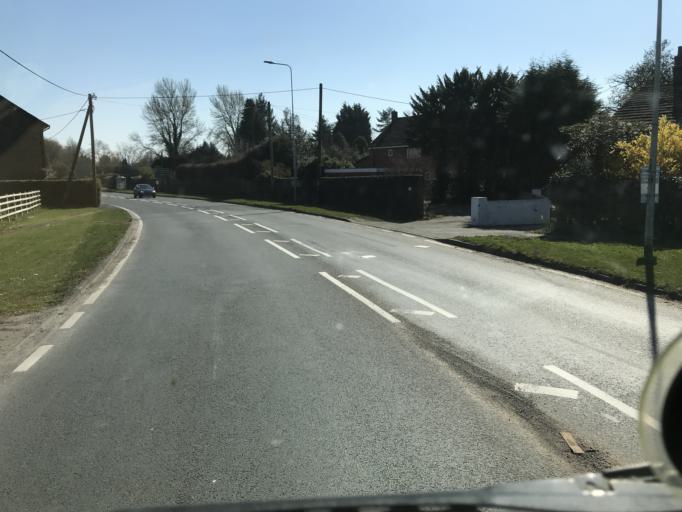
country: GB
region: England
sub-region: Cheshire East
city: Siddington
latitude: 53.2657
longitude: -2.2734
